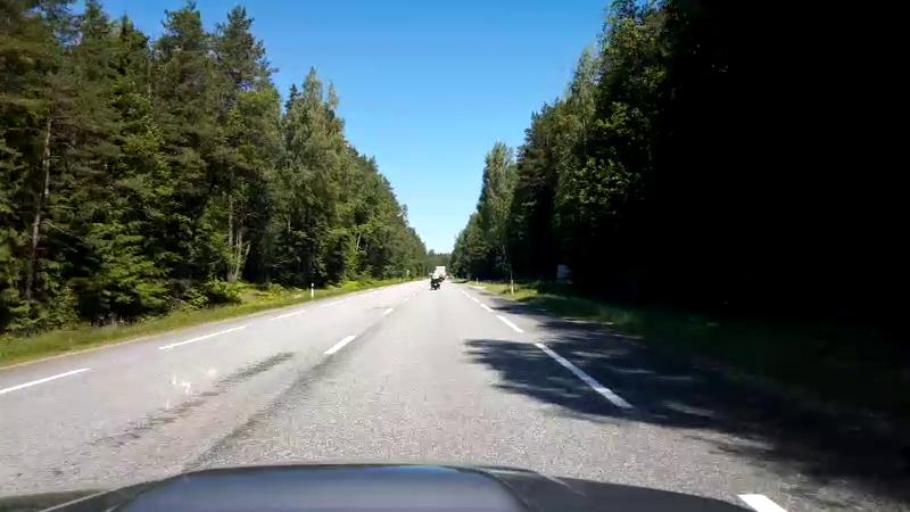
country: LV
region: Saulkrastu
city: Saulkrasti
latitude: 57.3957
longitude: 24.4283
